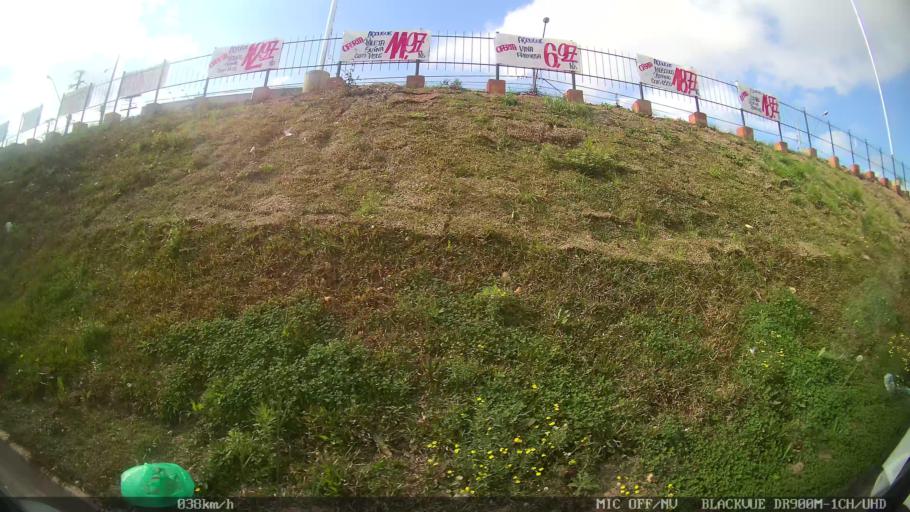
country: BR
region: Parana
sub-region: Pinhais
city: Pinhais
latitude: -25.3766
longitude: -49.1853
